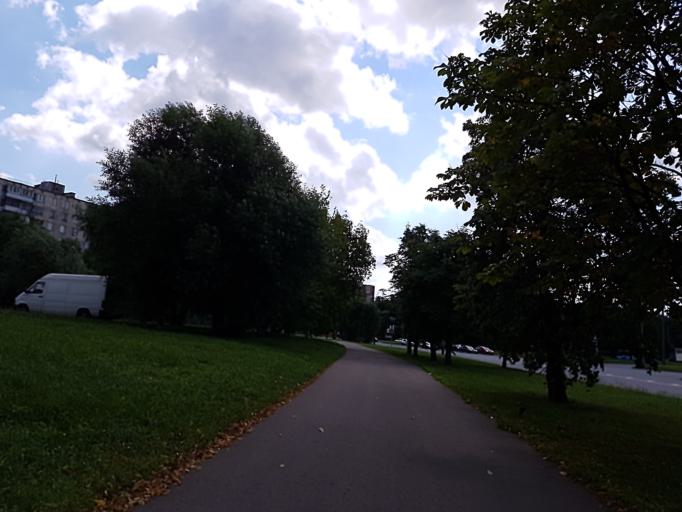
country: RU
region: Moskovskaya
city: Kuskovo
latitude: 55.7400
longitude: 37.8176
